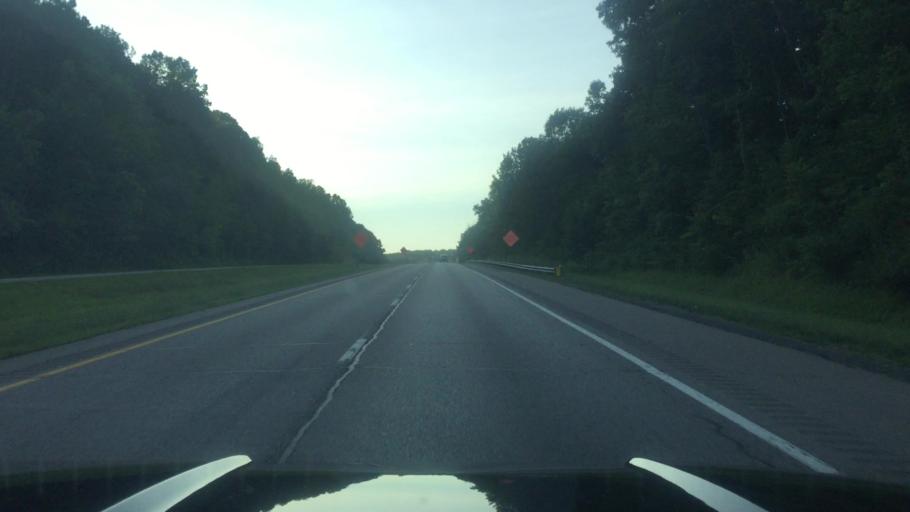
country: US
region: Ohio
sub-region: Tuscarawas County
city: Newcomerstown
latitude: 40.1689
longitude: -81.5476
